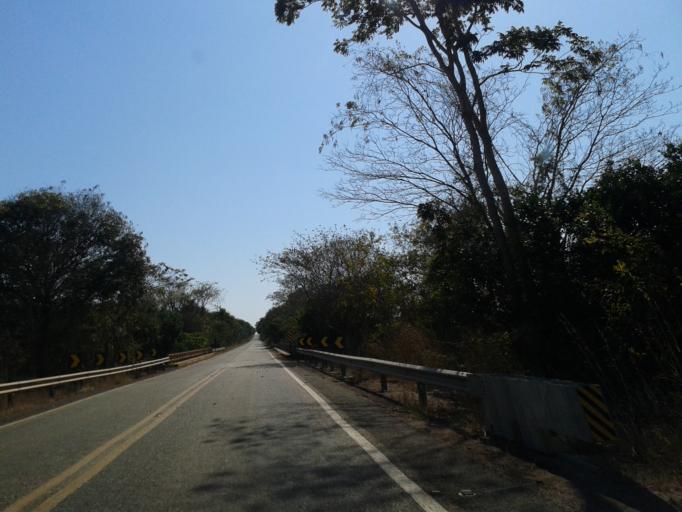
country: BR
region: Goias
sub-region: Mozarlandia
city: Mozarlandia
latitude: -14.4900
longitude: -50.4817
